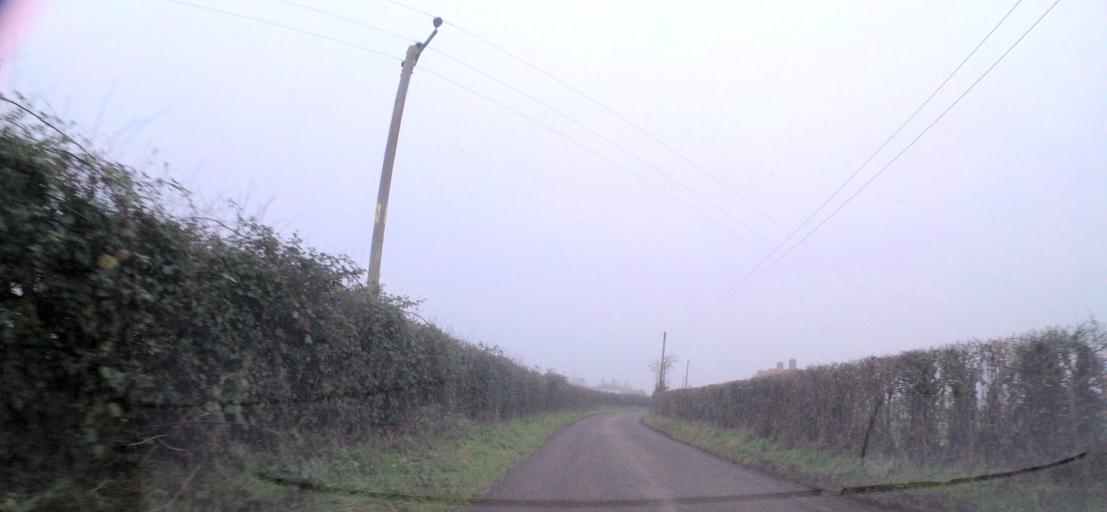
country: GB
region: England
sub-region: West Berkshire
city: Theale
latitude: 51.4078
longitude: -1.0990
